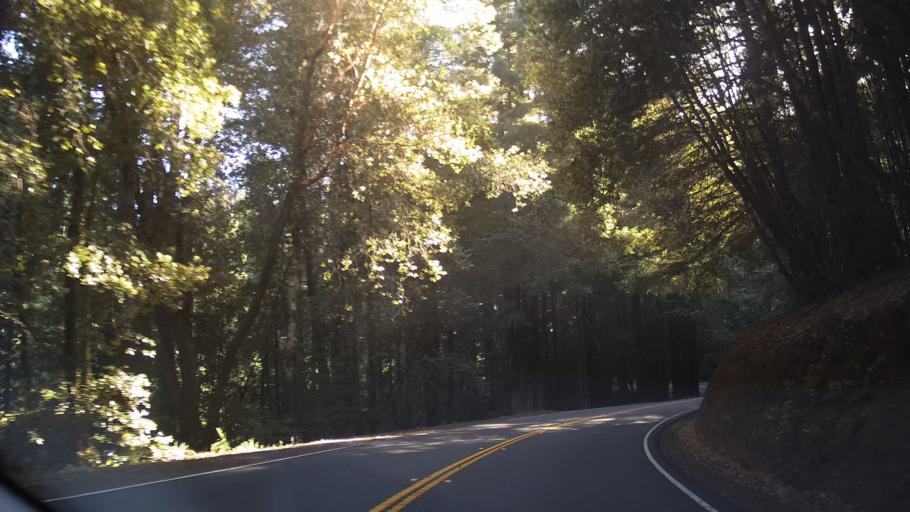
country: US
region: California
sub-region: Mendocino County
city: Fort Bragg
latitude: 39.3576
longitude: -123.6259
